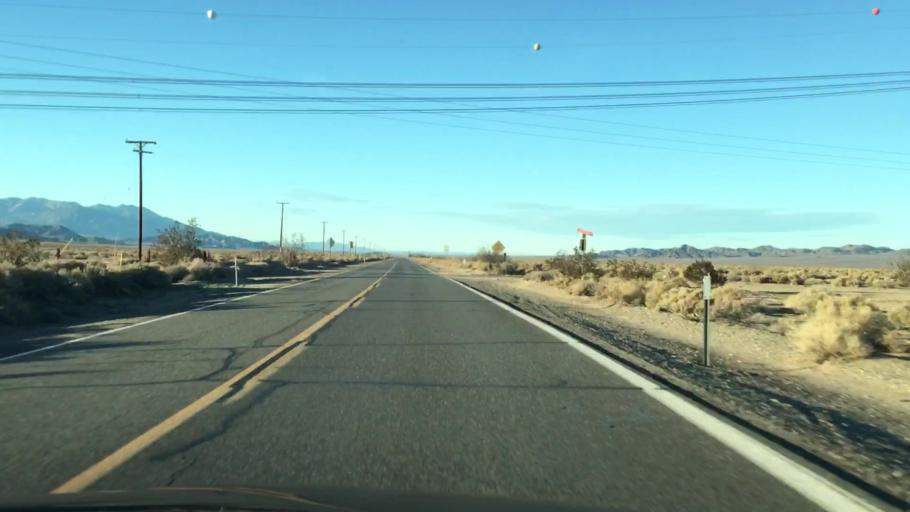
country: US
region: California
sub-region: San Bernardino County
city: Fort Irwin
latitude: 35.2779
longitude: -116.0753
